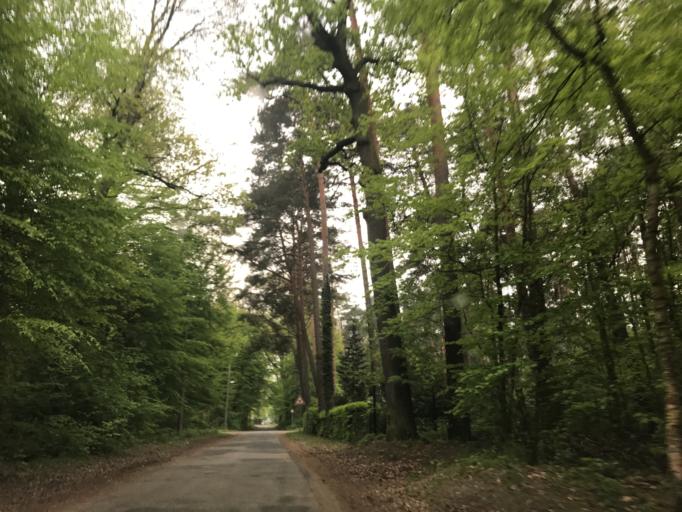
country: DE
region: Brandenburg
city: Falkensee
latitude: 52.6007
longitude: 13.1203
